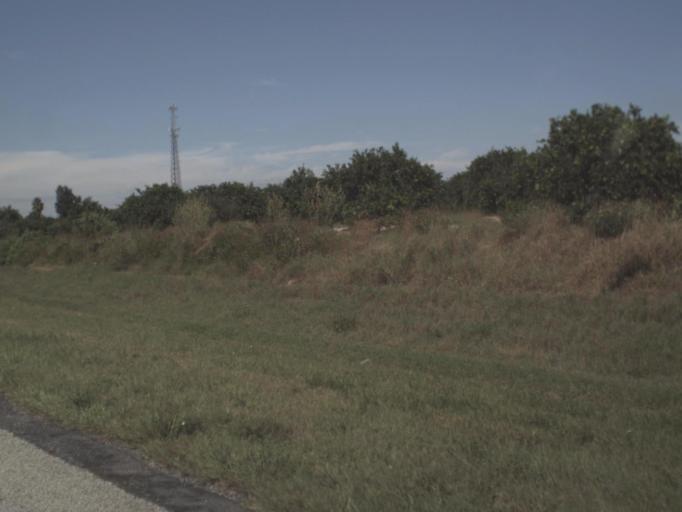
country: US
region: Florida
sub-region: Highlands County
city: Lake Placid
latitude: 27.3316
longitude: -81.3828
